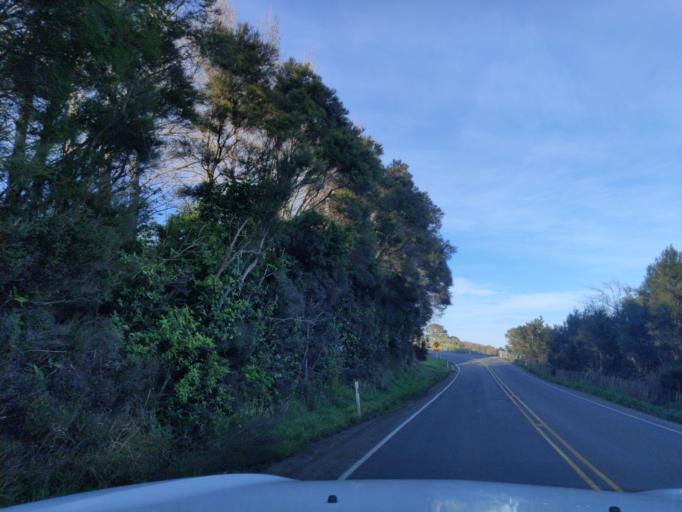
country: NZ
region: Manawatu-Wanganui
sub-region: Palmerston North City
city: Palmerston North
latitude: -40.2840
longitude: 175.7718
